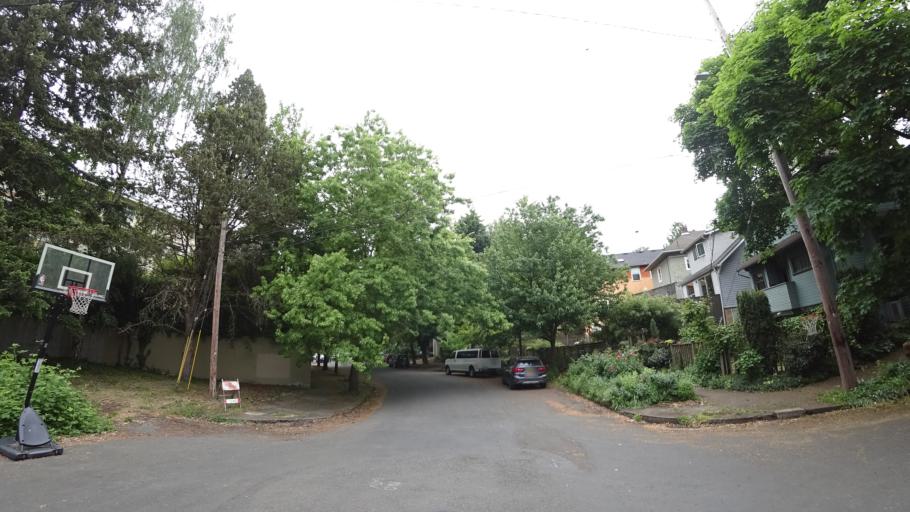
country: US
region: Oregon
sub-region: Multnomah County
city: Portland
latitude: 45.5182
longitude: -122.6324
